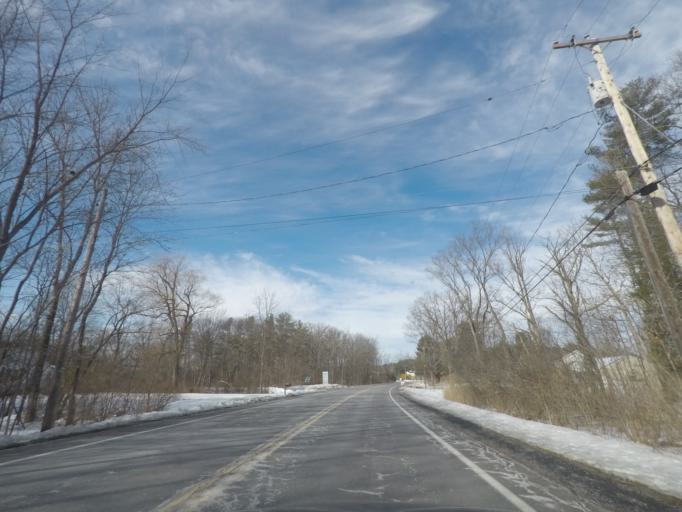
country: US
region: New York
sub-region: Albany County
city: Voorheesville
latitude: 42.6564
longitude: -73.9394
